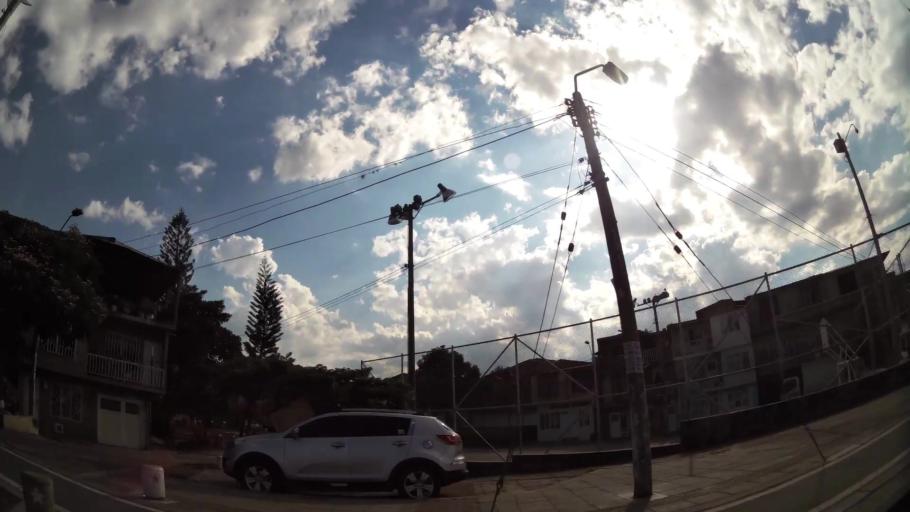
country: CO
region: Valle del Cauca
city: Cali
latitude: 3.4267
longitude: -76.4966
